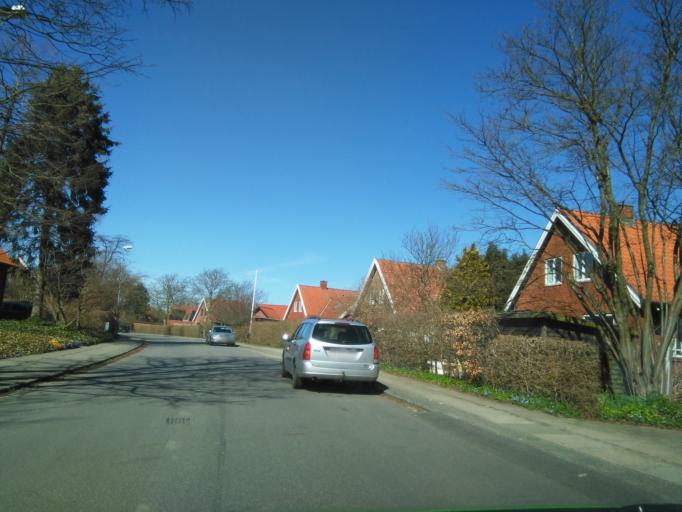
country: DK
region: Central Jutland
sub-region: Arhus Kommune
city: Arhus
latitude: 56.1940
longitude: 10.2276
